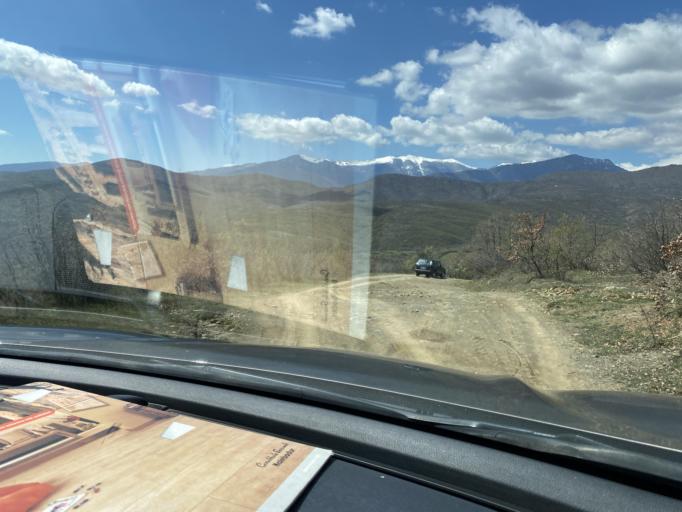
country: MK
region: Caska
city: Caska
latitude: 41.7312
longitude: 21.6556
